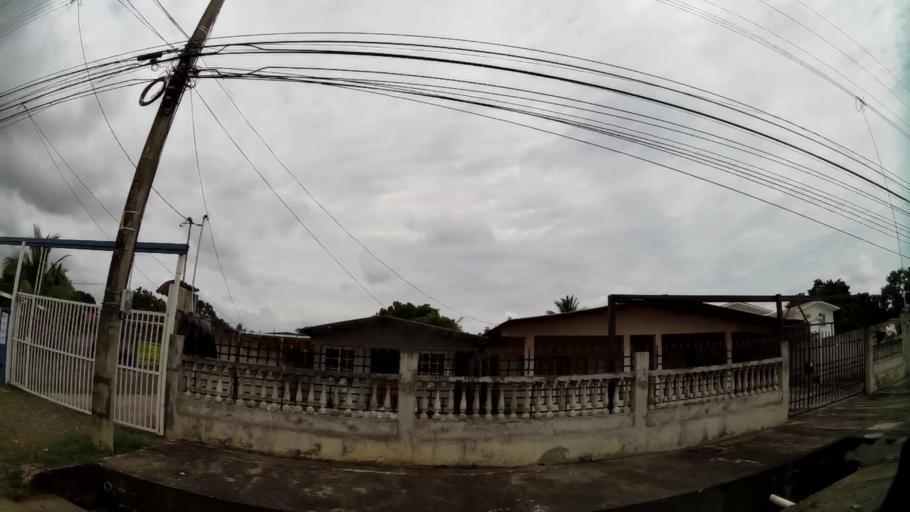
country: PA
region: Panama
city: San Miguelito
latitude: 9.0487
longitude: -79.4256
